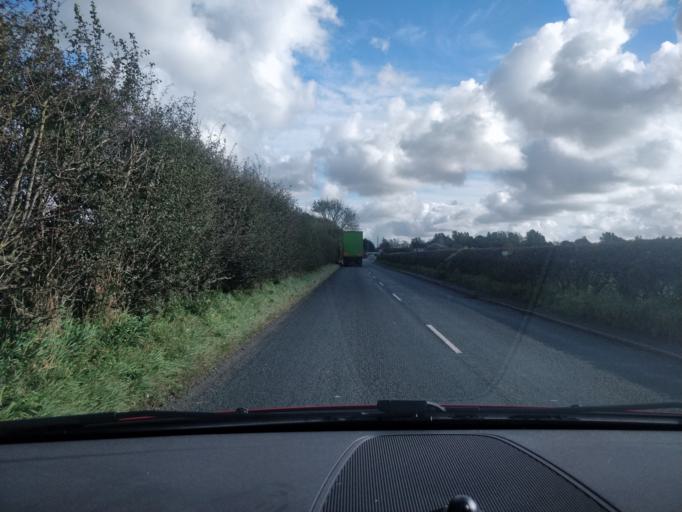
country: GB
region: England
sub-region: Lancashire
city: Ormskirk
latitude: 53.5884
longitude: -2.8699
